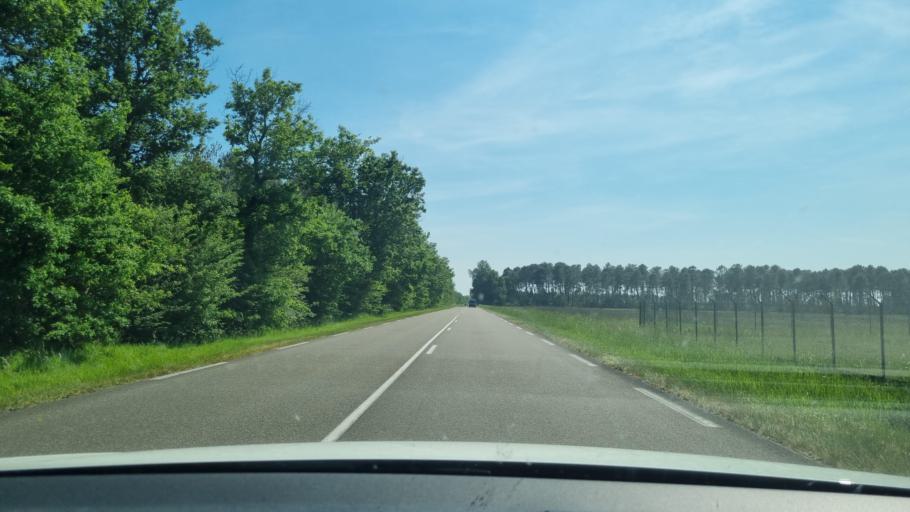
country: FR
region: Aquitaine
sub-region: Departement des Landes
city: Roquefort
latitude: 44.1833
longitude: -0.2763
